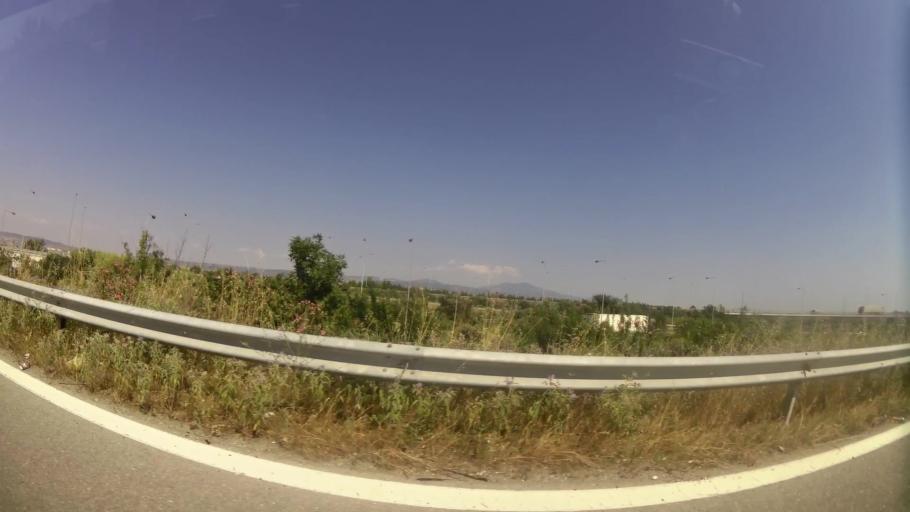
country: GR
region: Central Macedonia
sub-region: Nomos Thessalonikis
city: Kalochori
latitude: 40.6547
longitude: 22.8411
